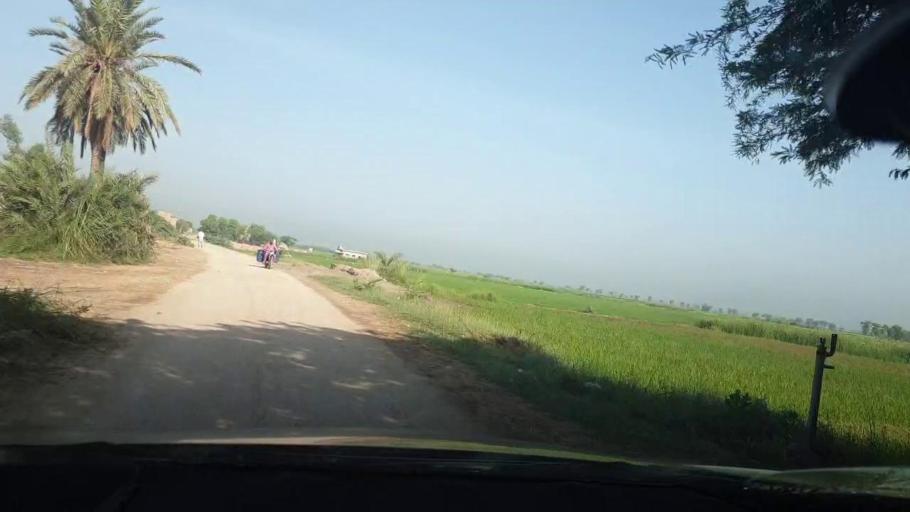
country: PK
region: Sindh
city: Kambar
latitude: 27.6541
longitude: 68.0333
